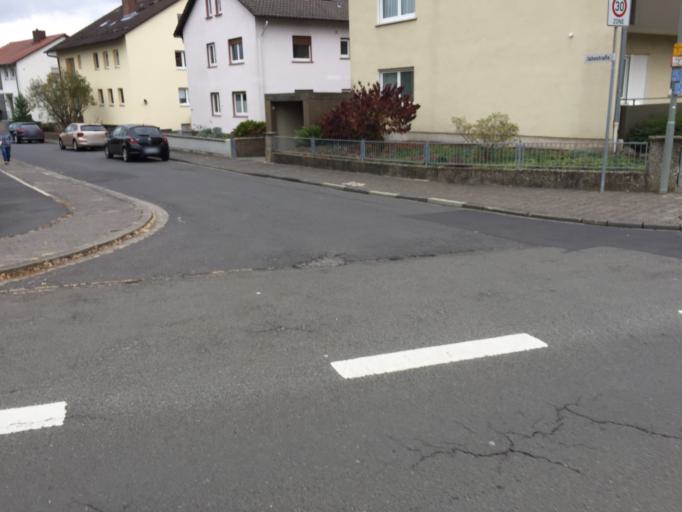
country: DE
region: Hesse
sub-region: Regierungsbezirk Giessen
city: Lich
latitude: 50.5220
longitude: 8.8092
